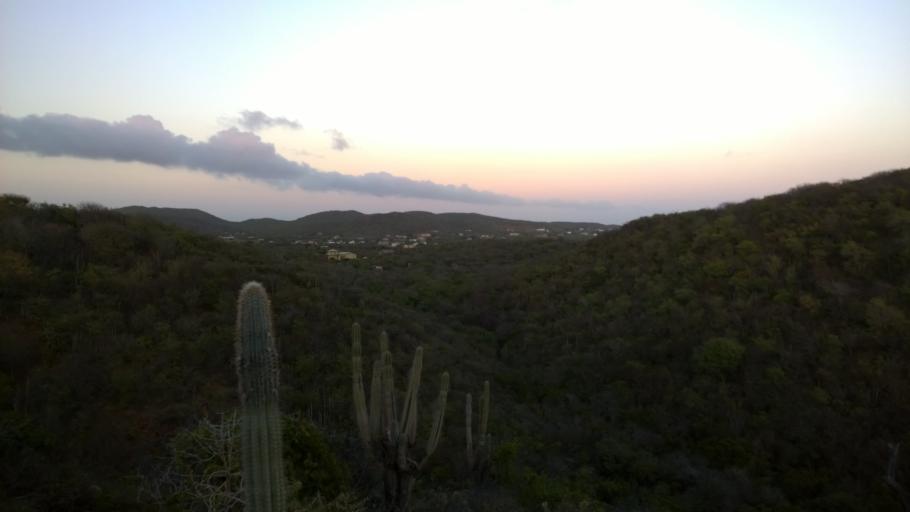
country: CW
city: Dorp Soto
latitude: 12.2594
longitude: -69.1064
